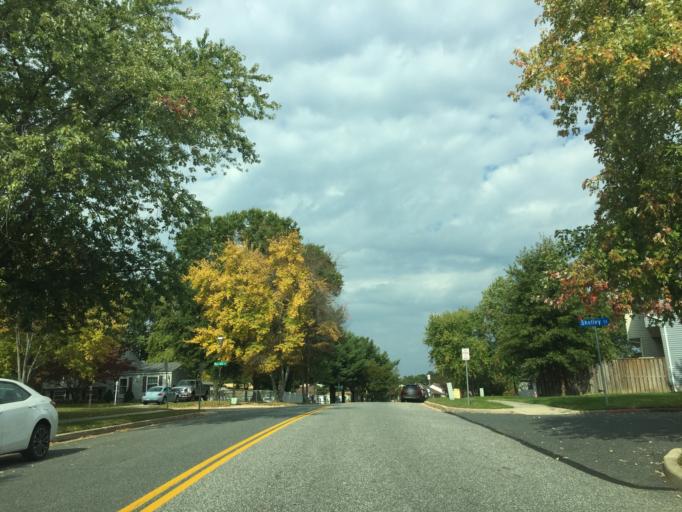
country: US
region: Maryland
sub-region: Harford County
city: Bel Air South
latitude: 39.4775
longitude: -76.3076
